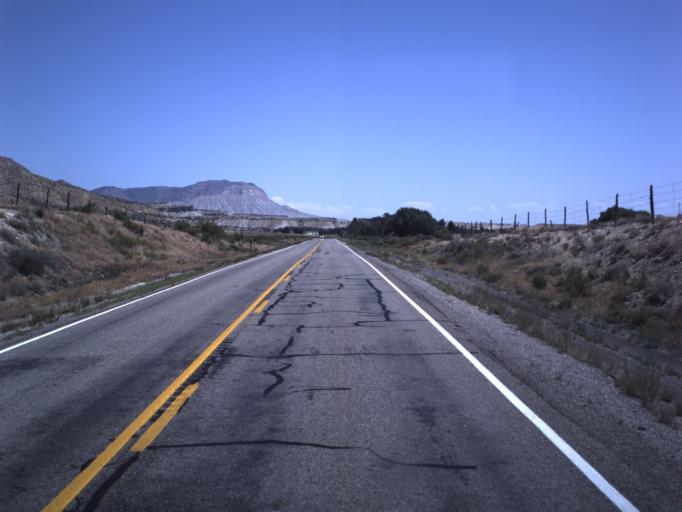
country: US
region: Utah
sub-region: Emery County
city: Ferron
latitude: 38.9127
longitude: -111.2665
